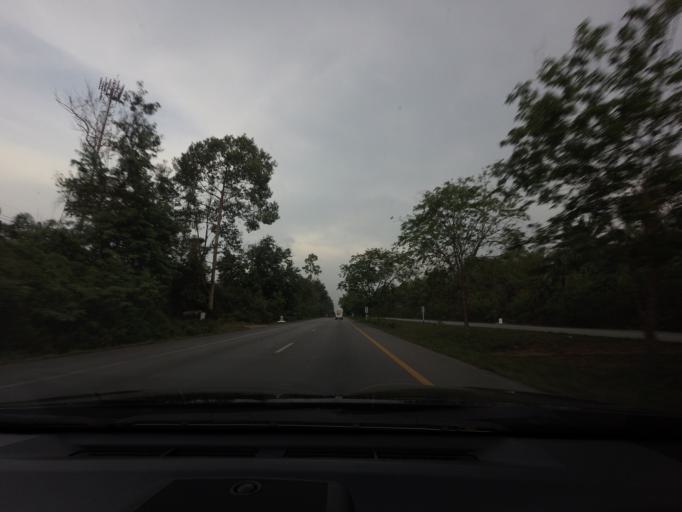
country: TH
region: Surat Thani
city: Tha Chana
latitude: 9.4751
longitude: 99.1470
